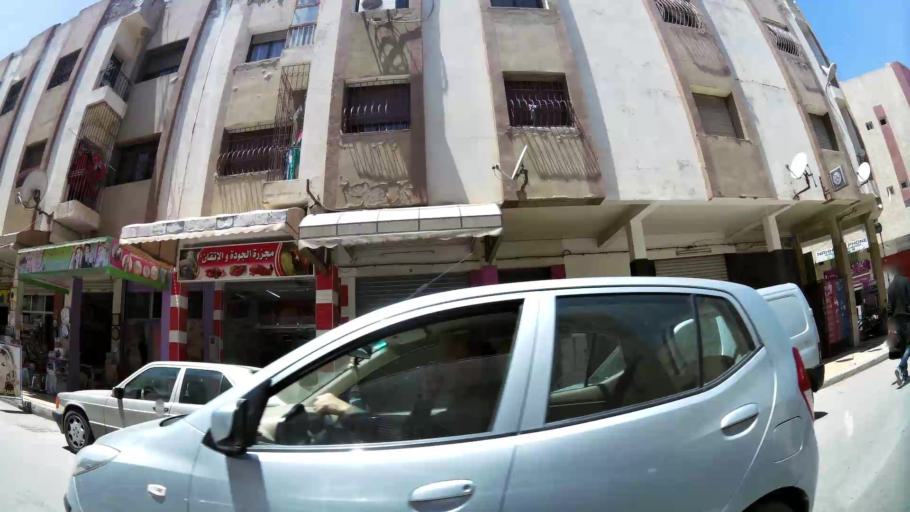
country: MA
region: Fes-Boulemane
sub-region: Fes
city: Fes
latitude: 34.0224
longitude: -5.0093
